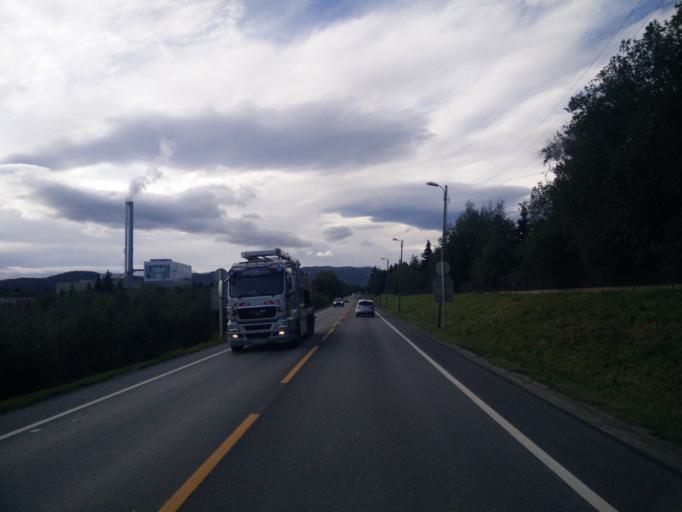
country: NO
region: Sor-Trondelag
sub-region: Trondheim
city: Trondheim
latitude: 63.3521
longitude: 10.3698
